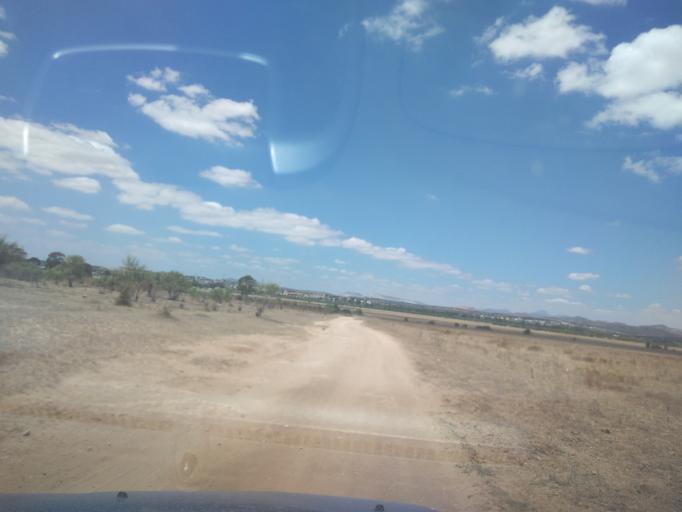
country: TN
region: Susah
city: Harqalah
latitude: 36.1676
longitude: 10.4365
